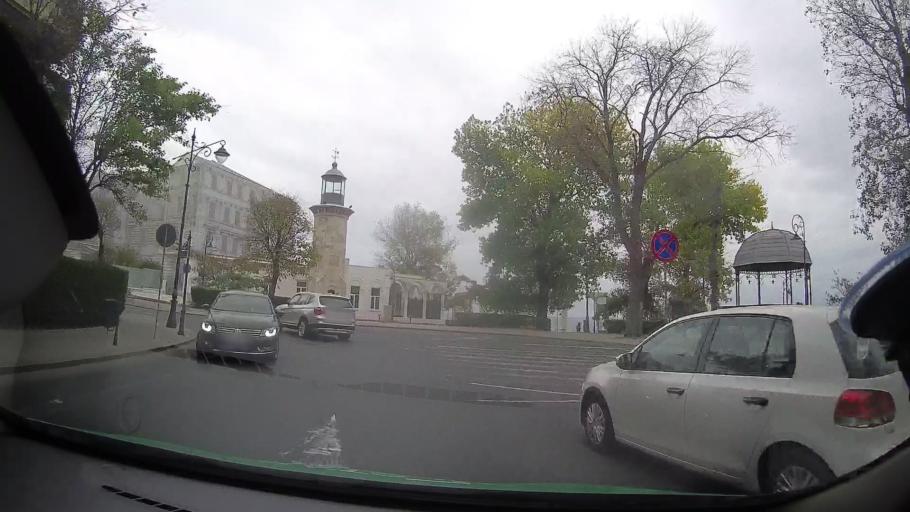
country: RO
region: Constanta
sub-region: Municipiul Constanta
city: Constanta
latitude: 44.1718
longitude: 28.6642
